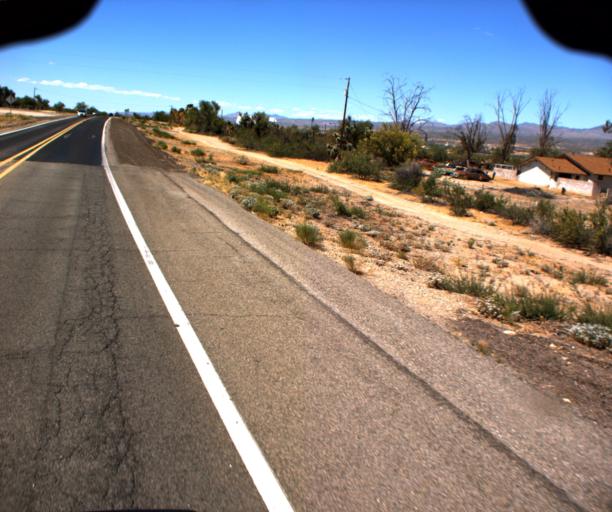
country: US
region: Arizona
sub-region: Yavapai County
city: Bagdad
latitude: 34.7149
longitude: -113.6143
